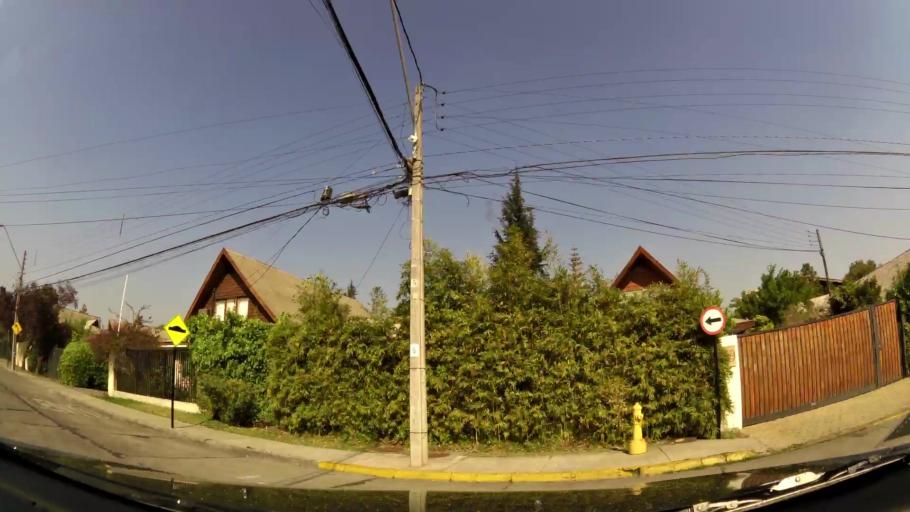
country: CL
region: Santiago Metropolitan
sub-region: Provincia de Santiago
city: Villa Presidente Frei, Nunoa, Santiago, Chile
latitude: -33.3953
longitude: -70.5699
